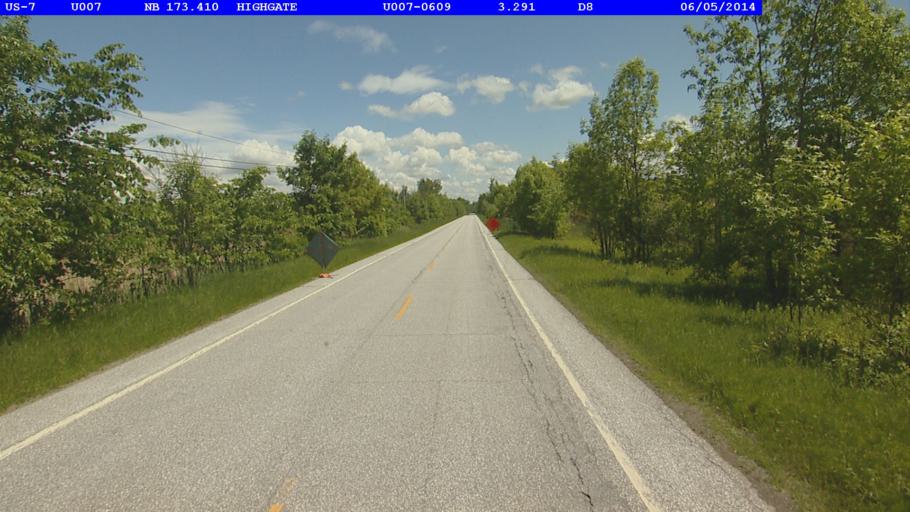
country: US
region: Vermont
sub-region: Franklin County
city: Swanton
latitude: 44.9783
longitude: -73.1005
